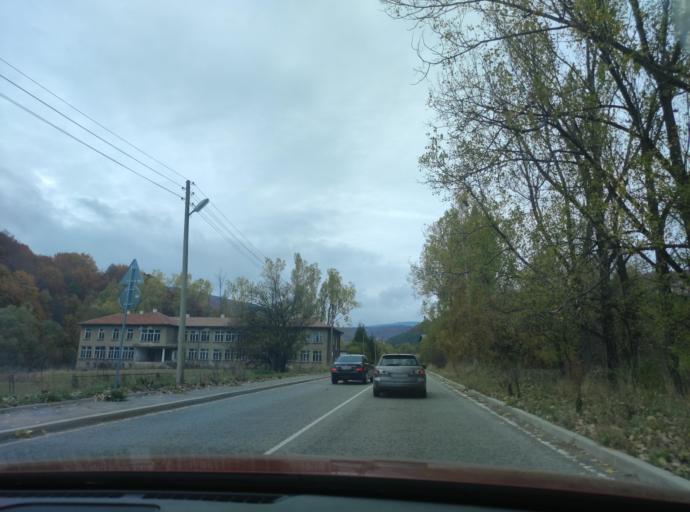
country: BG
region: Sofiya
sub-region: Obshtina Godech
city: Godech
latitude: 43.0795
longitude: 23.1067
